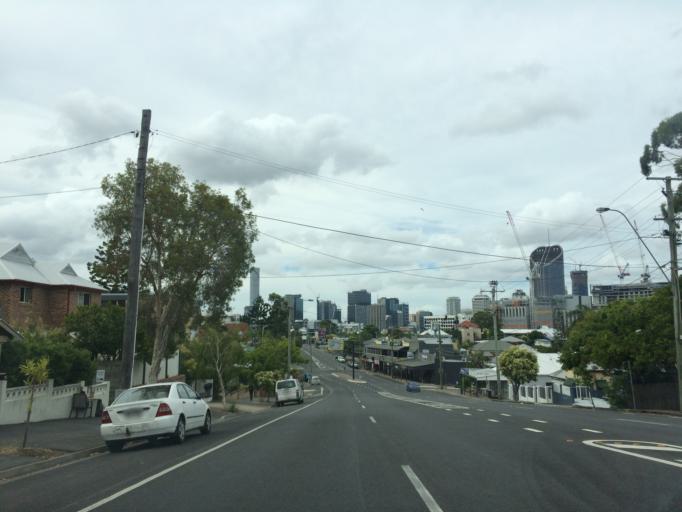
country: AU
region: Queensland
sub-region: Brisbane
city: South Brisbane
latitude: -27.4860
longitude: 153.0194
